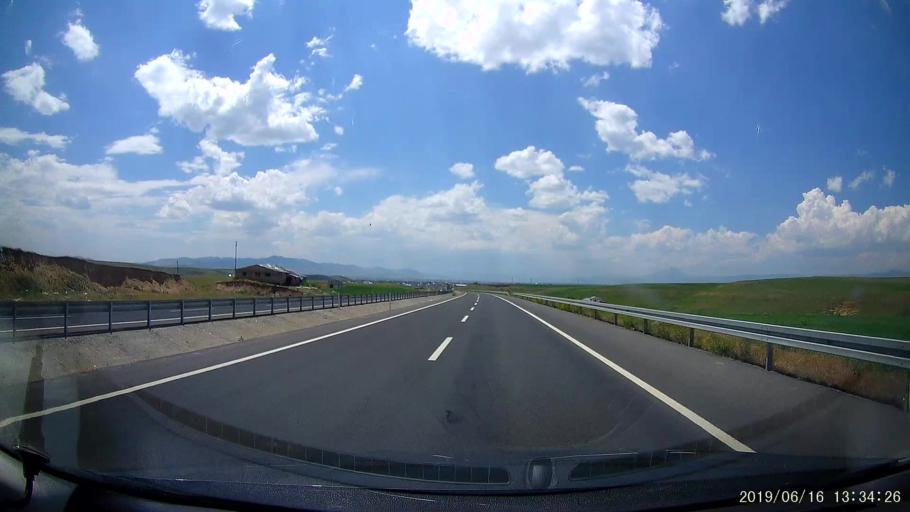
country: TR
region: Agri
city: Agri
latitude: 39.7127
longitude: 43.1267
